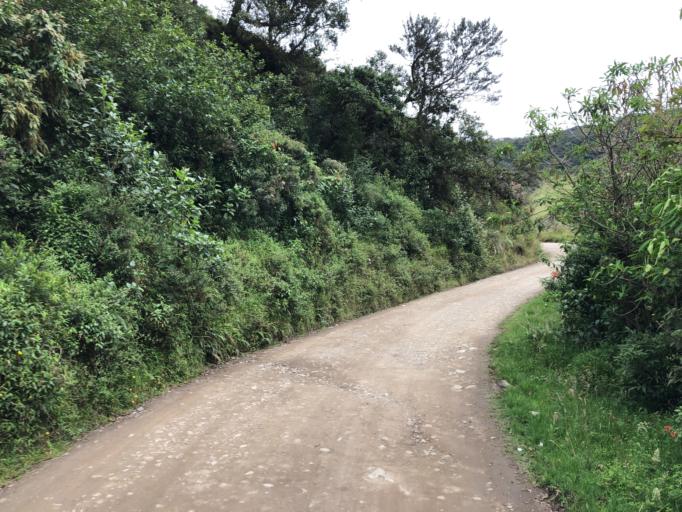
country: CO
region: Cauca
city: Totoro
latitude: 2.5105
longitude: -76.3666
